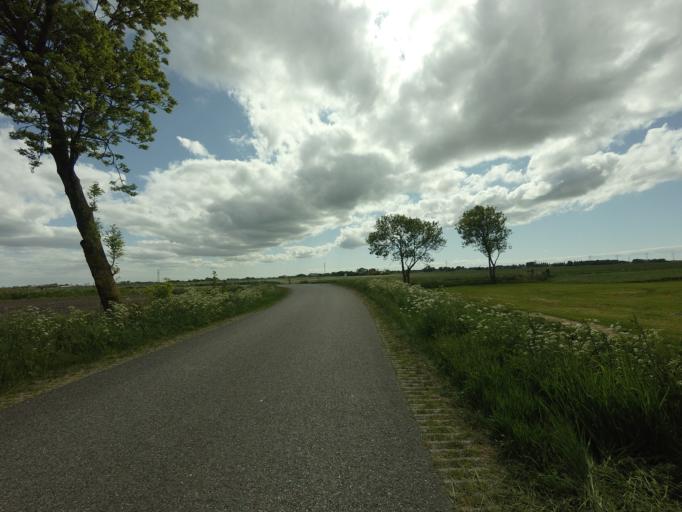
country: NL
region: Friesland
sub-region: Sudwest Fryslan
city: Bolsward
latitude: 53.0785
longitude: 5.5509
